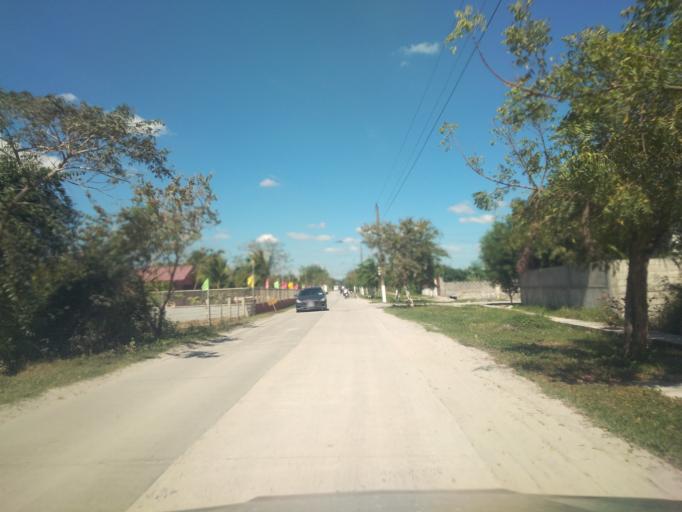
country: PH
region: Central Luzon
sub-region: Province of Pampanga
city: Balas
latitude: 15.0380
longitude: 120.6194
